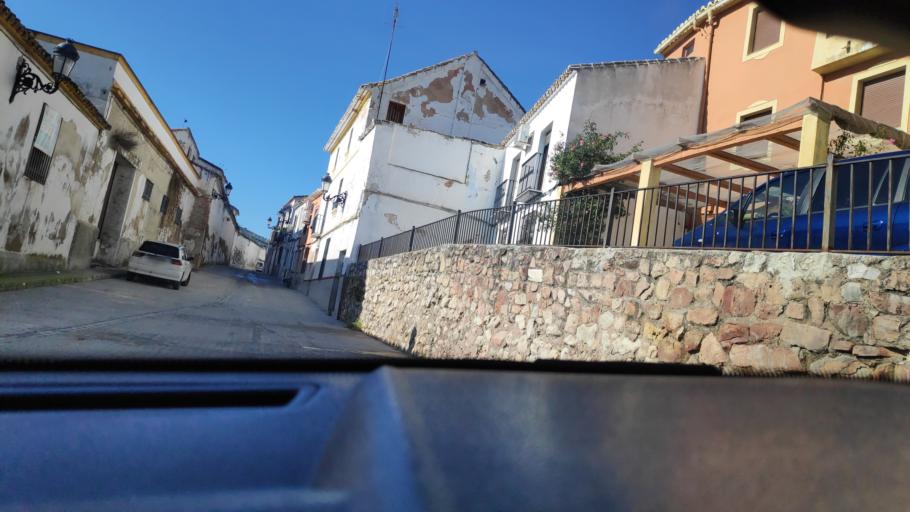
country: ES
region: Andalusia
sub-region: Province of Cordoba
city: Baena
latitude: 37.6120
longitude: -4.3236
